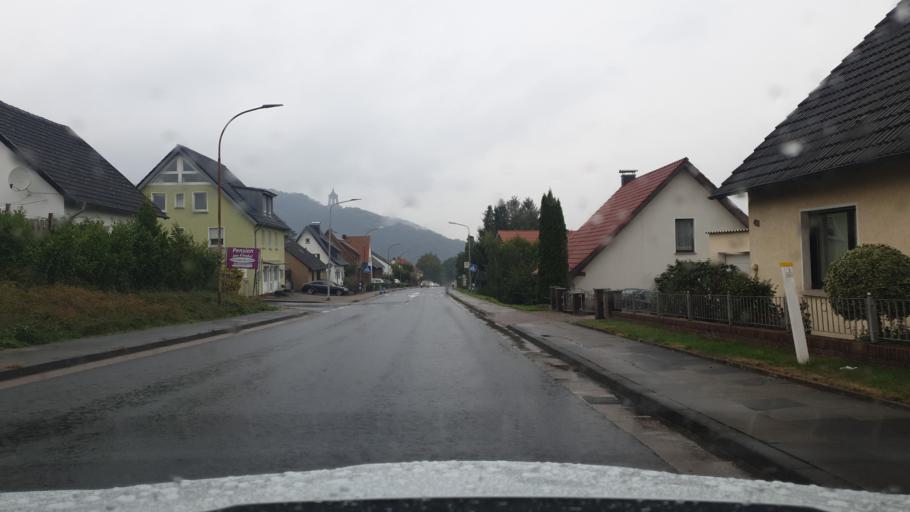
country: DE
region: North Rhine-Westphalia
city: Porta Westfalica
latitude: 52.2296
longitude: 8.9145
